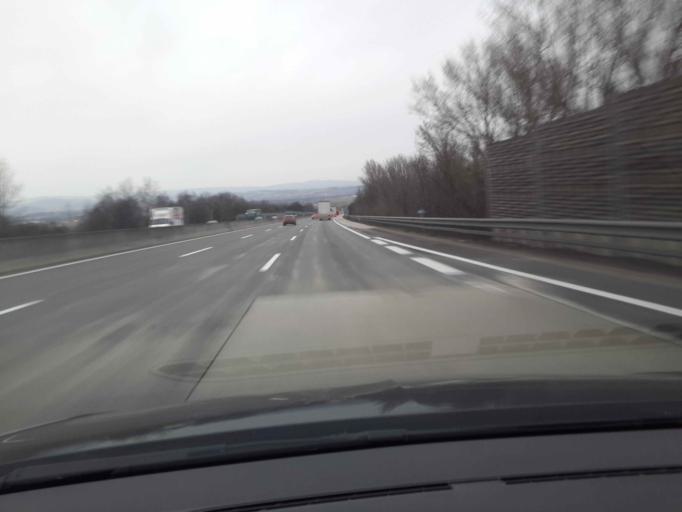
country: AT
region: Lower Austria
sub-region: Politischer Bezirk Amstetten
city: Sankt Valentin
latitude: 48.1672
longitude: 14.5507
